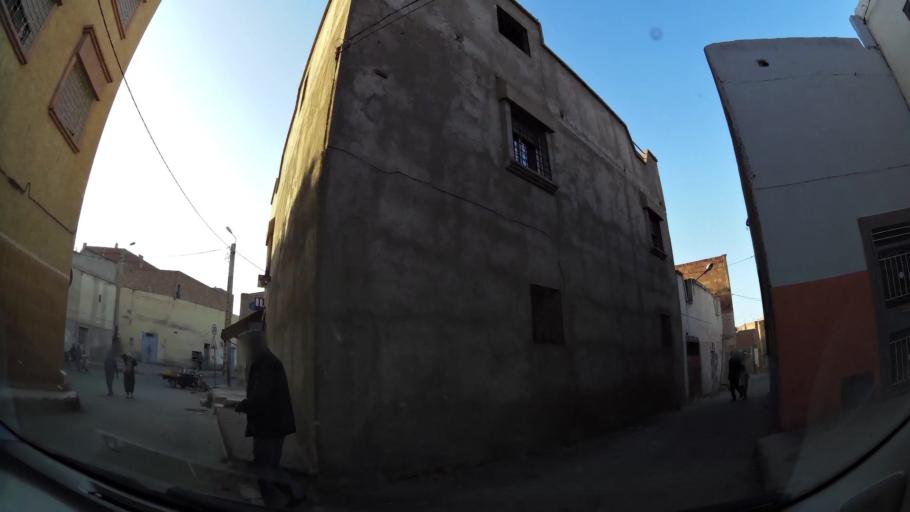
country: MA
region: Oriental
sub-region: Oujda-Angad
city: Oujda
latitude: 34.7064
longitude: -1.9096
